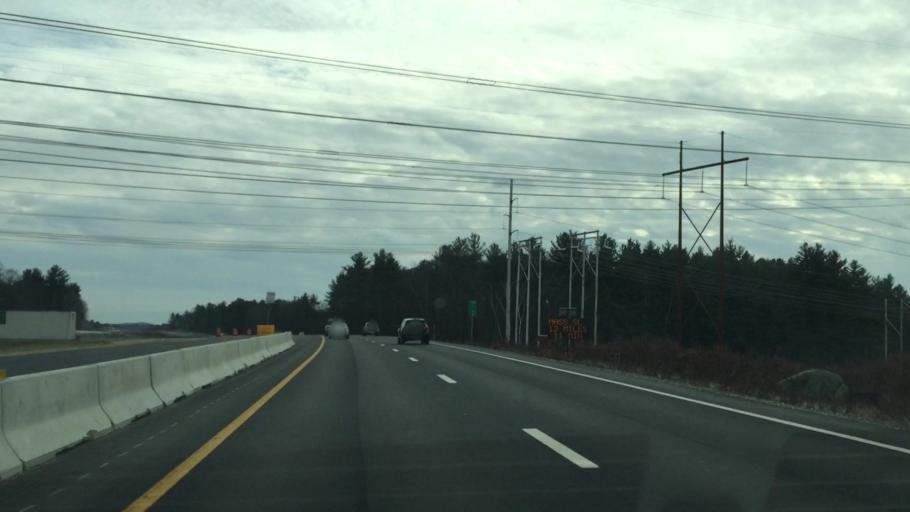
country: US
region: New Hampshire
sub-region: Rockingham County
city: Londonderry
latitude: 42.8966
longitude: -71.3612
